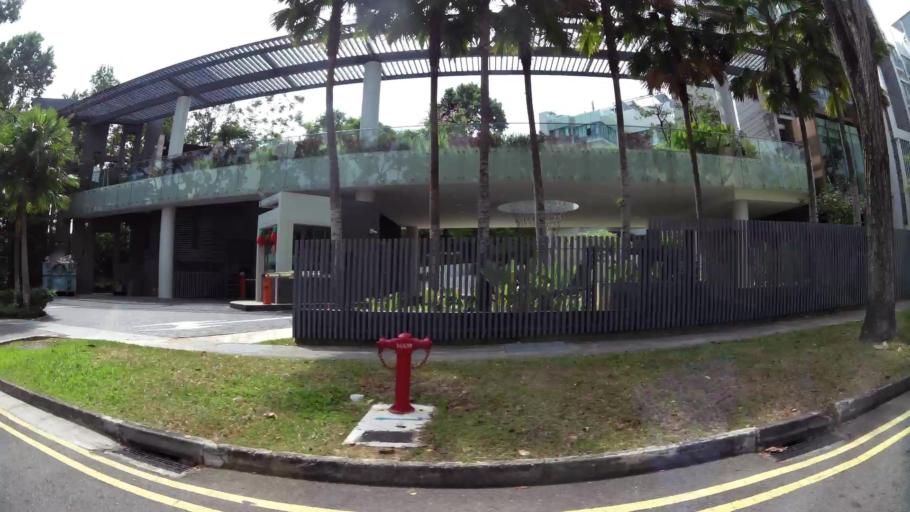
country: SG
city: Singapore
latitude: 1.3395
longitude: 103.7677
